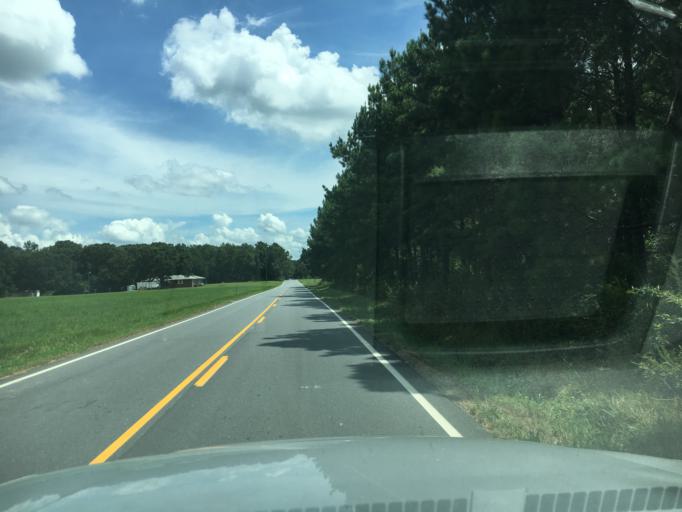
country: US
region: South Carolina
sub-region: Anderson County
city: Belton
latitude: 34.5324
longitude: -82.4341
